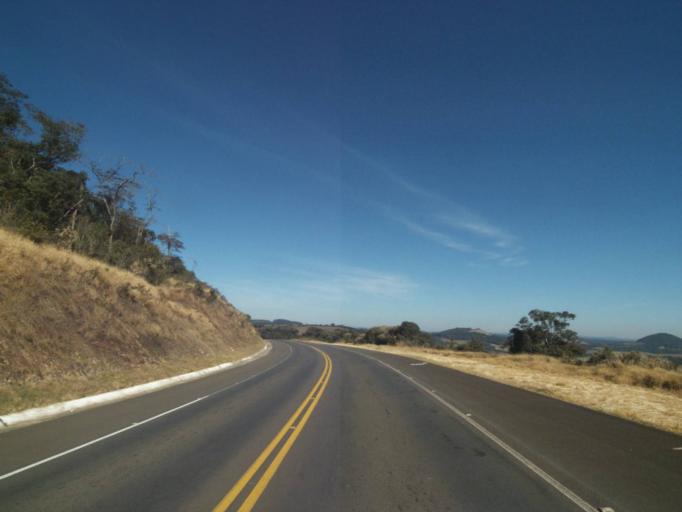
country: BR
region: Parana
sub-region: Tibagi
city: Tibagi
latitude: -24.7816
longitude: -50.4667
